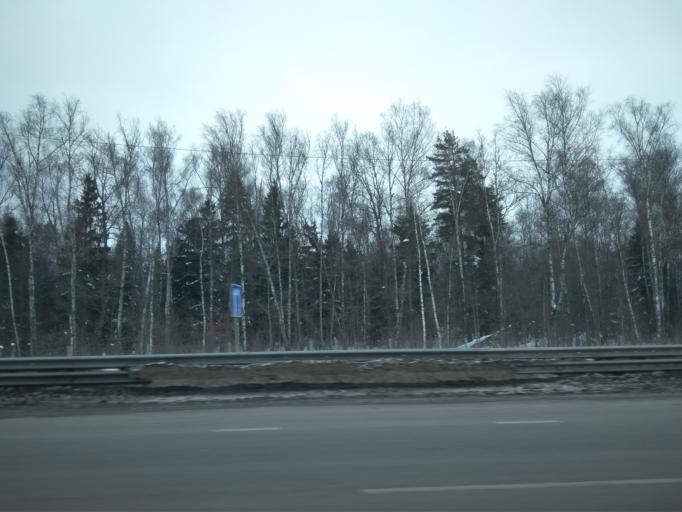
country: RU
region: Moskovskaya
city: Vostryakovo
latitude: 55.4370
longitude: 37.8730
